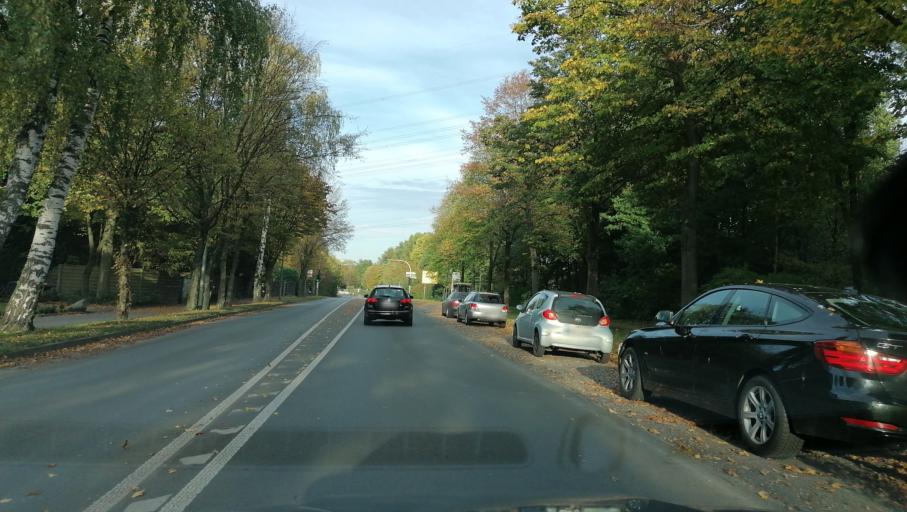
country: DE
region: North Rhine-Westphalia
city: Herten
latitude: 51.5871
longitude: 7.1137
